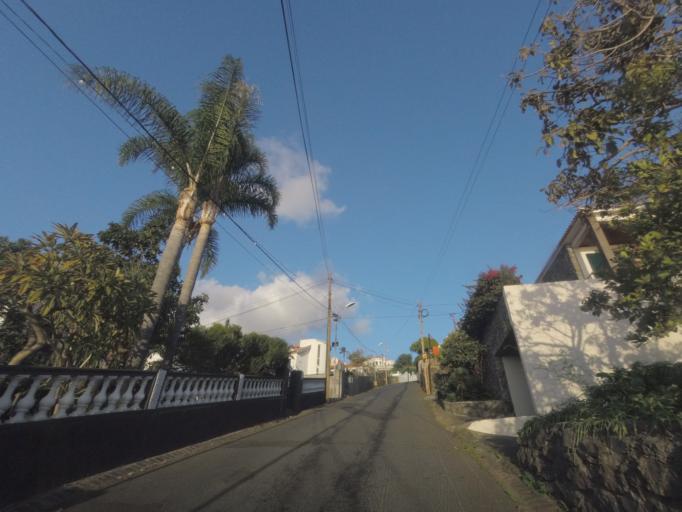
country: PT
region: Madeira
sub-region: Funchal
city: Funchal
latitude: 32.6490
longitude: -16.8845
